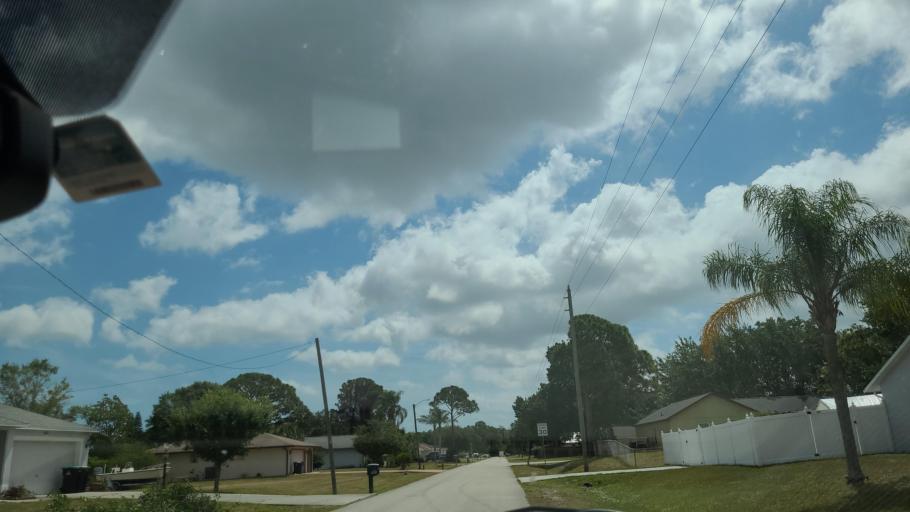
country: US
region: Florida
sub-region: Brevard County
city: West Melbourne
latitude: 28.0031
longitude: -80.6629
